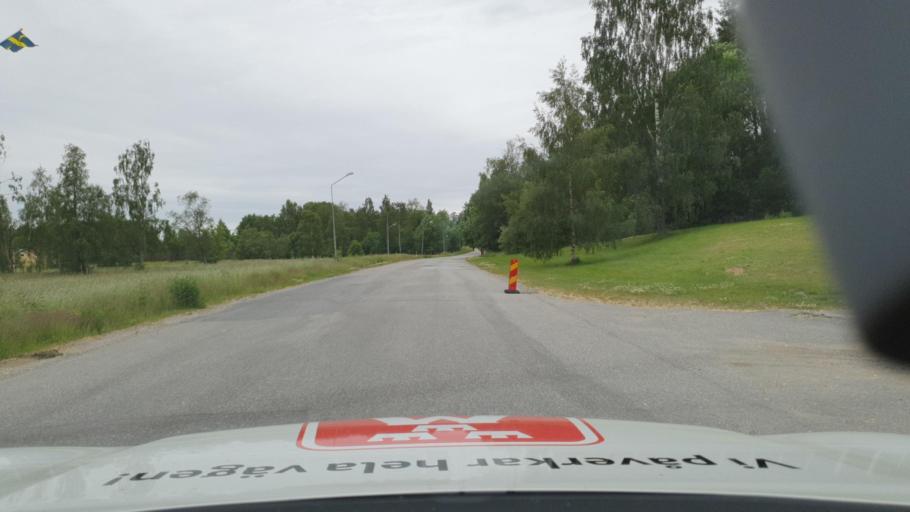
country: SE
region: Vaesterbotten
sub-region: Nordmalings Kommun
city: Nordmaling
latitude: 63.5379
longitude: 19.4434
